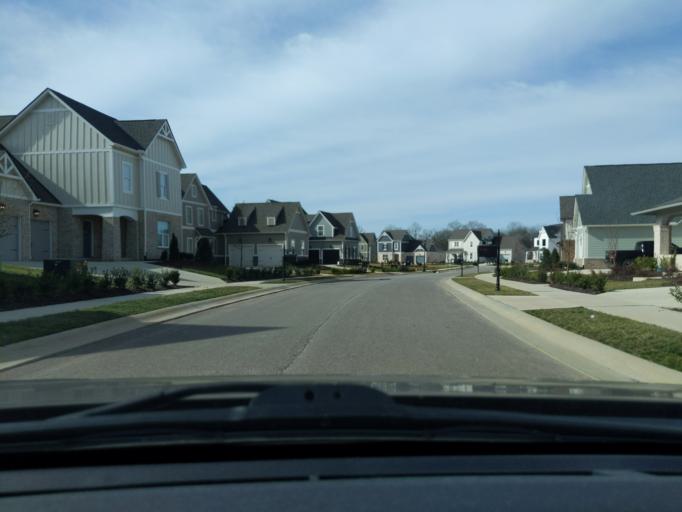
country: US
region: Tennessee
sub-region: Wilson County
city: Mount Juliet
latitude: 36.2084
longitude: -86.4915
